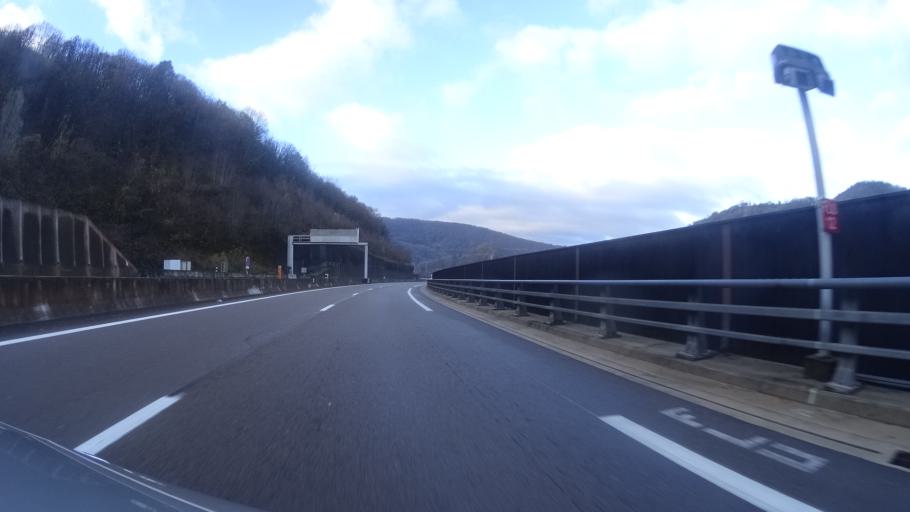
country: FR
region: Franche-Comte
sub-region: Departement du Doubs
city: Beure
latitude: 47.2156
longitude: 6.0096
